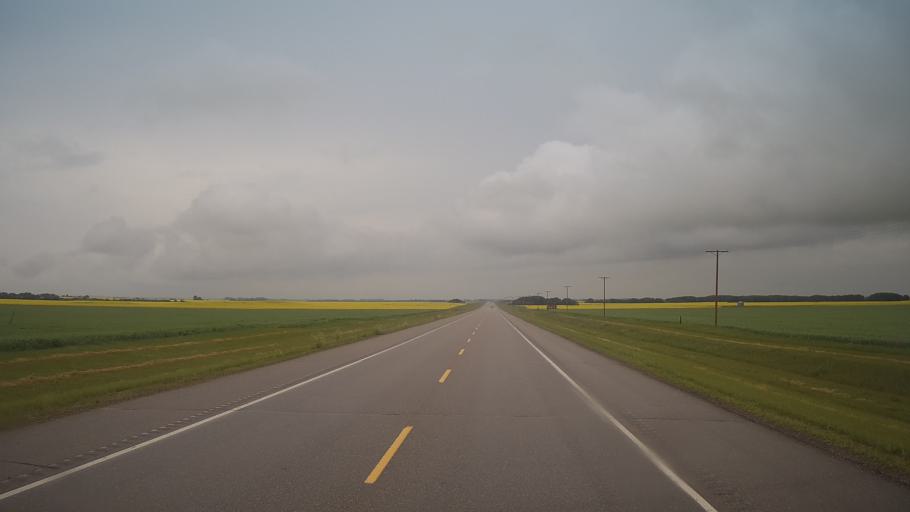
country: CA
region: Saskatchewan
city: Wilkie
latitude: 52.4224
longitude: -108.8999
